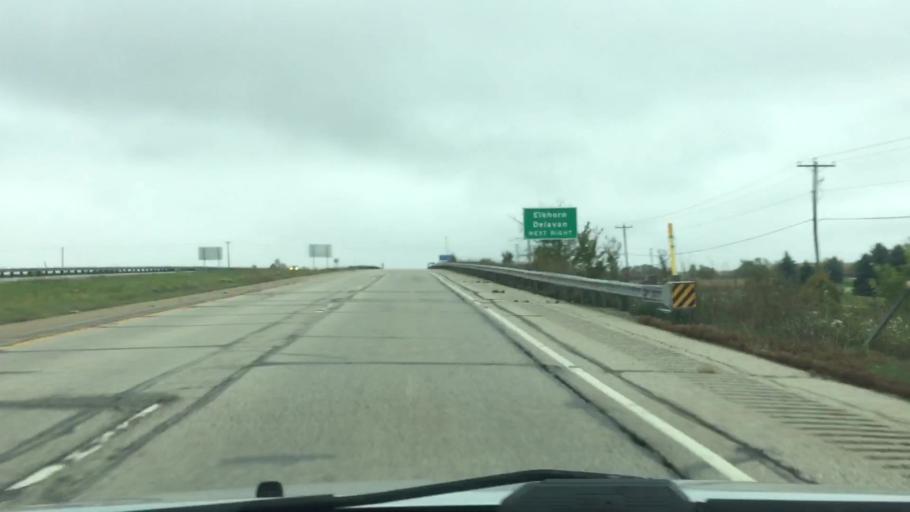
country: US
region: Wisconsin
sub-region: Walworth County
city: Elkhorn
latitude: 42.6852
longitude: -88.5296
